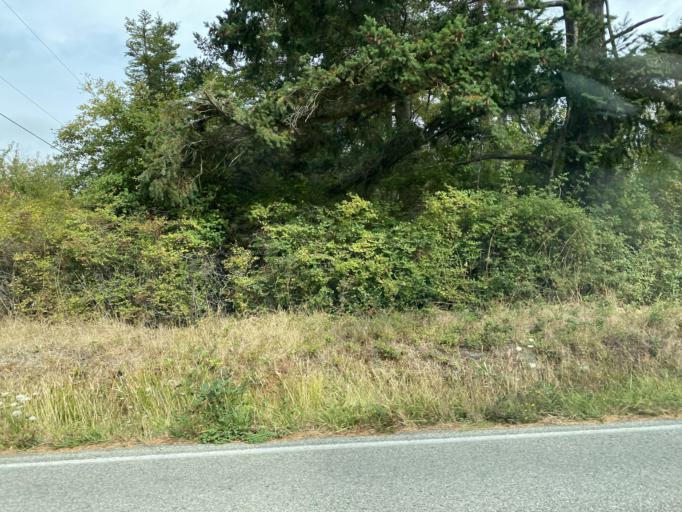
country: US
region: Washington
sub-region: Island County
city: Coupeville
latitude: 48.2391
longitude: -122.6901
